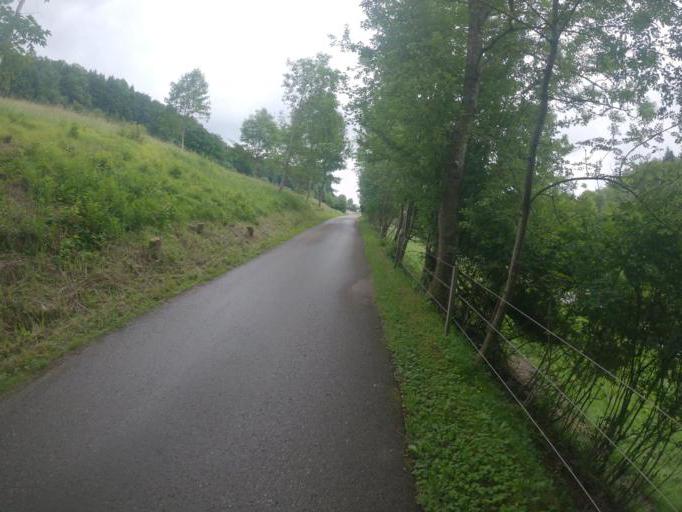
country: DE
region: Baden-Wuerttemberg
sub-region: Regierungsbezirk Stuttgart
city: Ebersbach an der Fils
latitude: 48.7469
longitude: 9.5402
